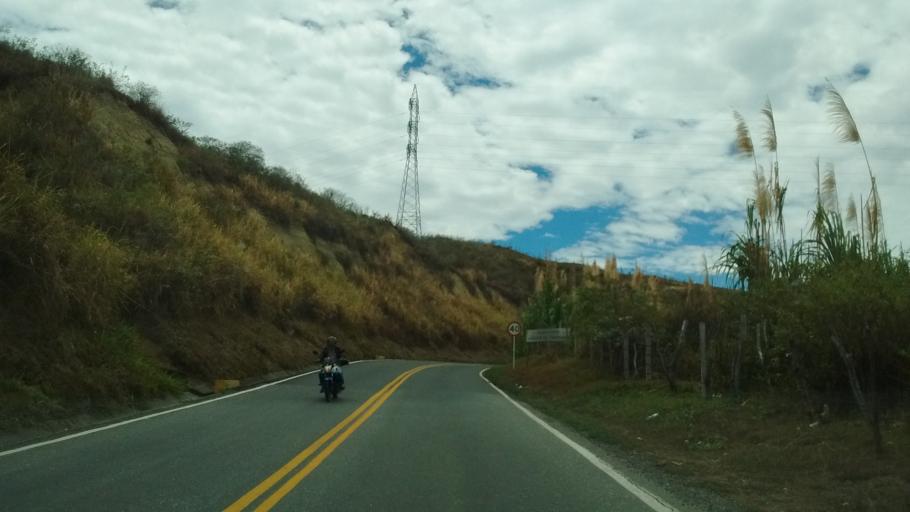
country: CO
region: Cauca
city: La Sierra
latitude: 2.2260
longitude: -76.7956
